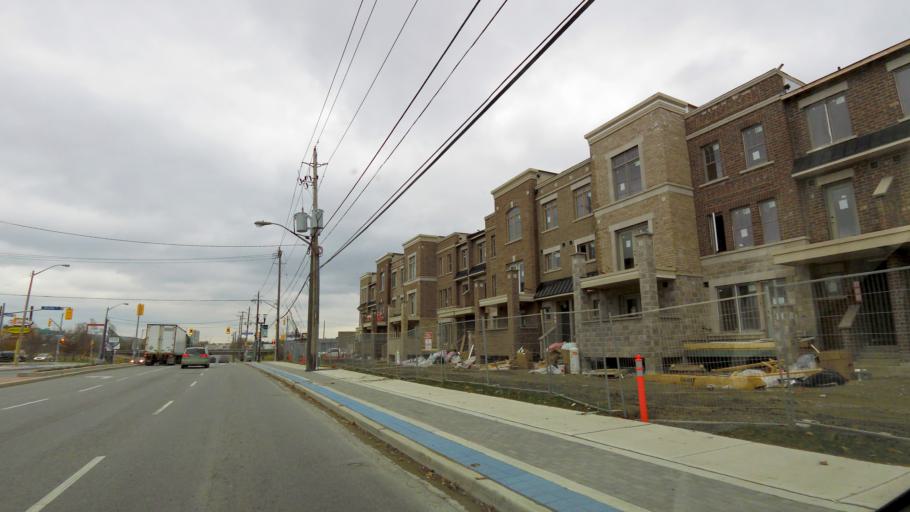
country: CA
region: Ontario
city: Concord
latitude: 43.7345
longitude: -79.5349
